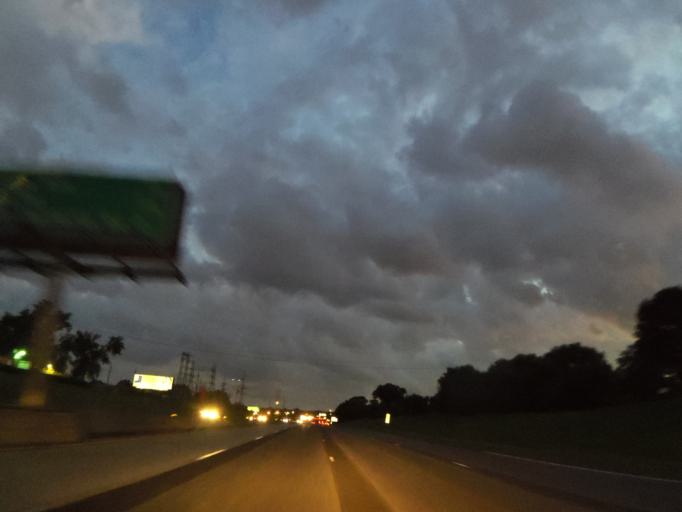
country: US
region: Missouri
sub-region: Saint Louis County
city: Lemay
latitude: 38.5511
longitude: -90.2822
